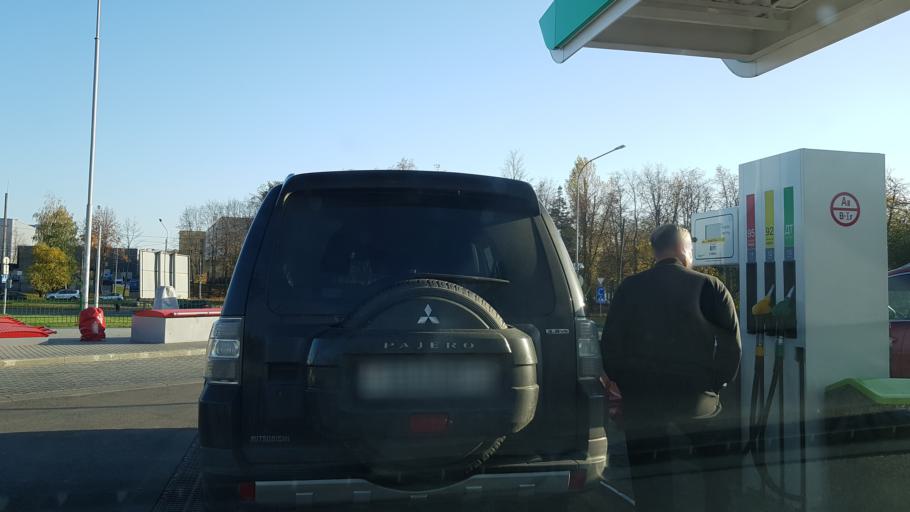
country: BY
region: Minsk
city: Syenitsa
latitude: 53.8784
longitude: 27.5141
